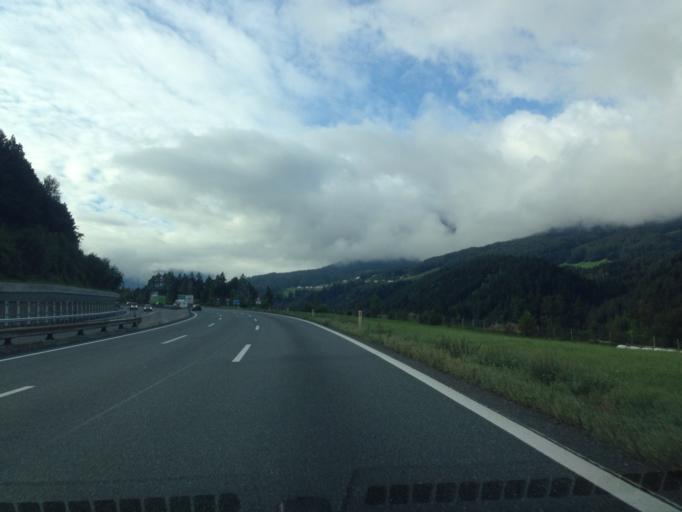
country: AT
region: Tyrol
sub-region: Politischer Bezirk Innsbruck Land
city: Mutters
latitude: 47.2255
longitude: 11.3921
